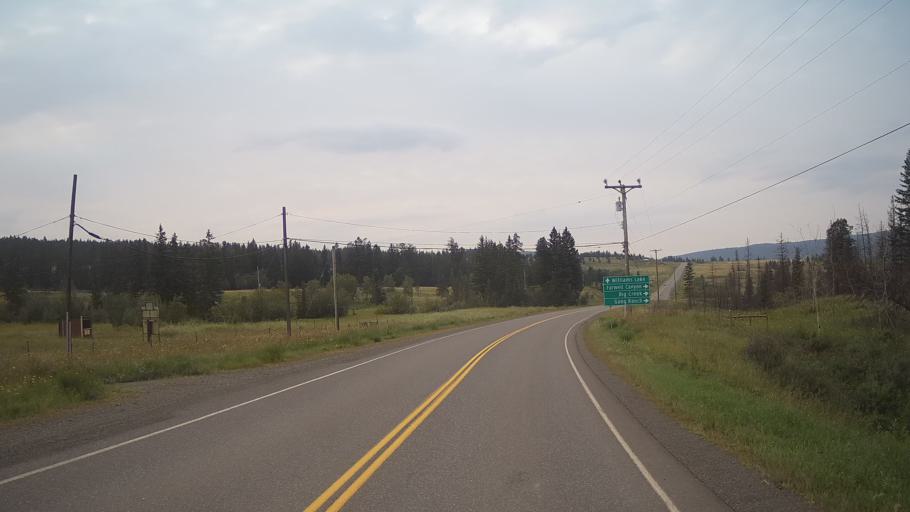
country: CA
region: British Columbia
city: Williams Lake
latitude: 51.9685
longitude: -122.5299
